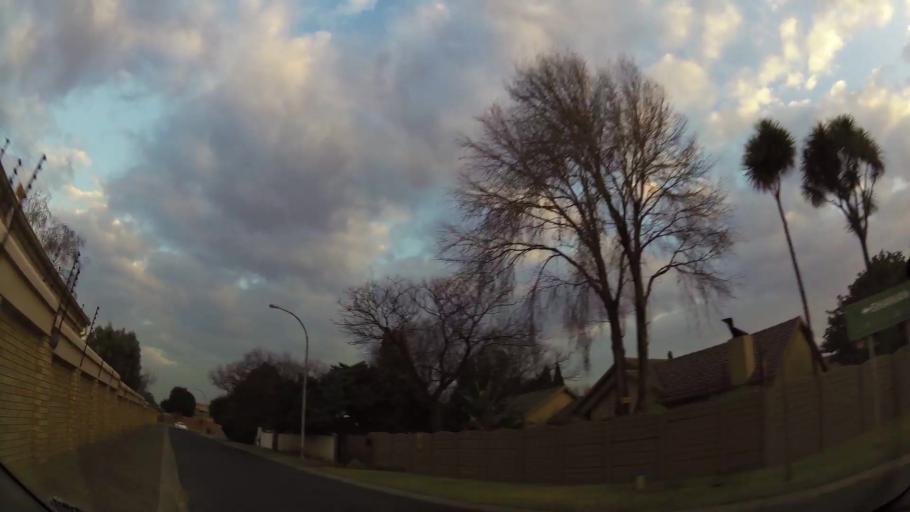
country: ZA
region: Gauteng
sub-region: Ekurhuleni Metropolitan Municipality
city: Benoni
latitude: -26.1695
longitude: 28.3070
